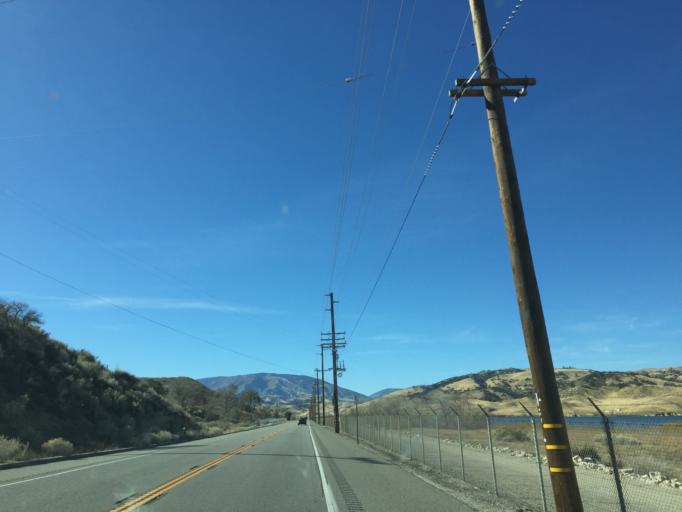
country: US
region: California
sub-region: Kern County
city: Lebec
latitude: 34.7686
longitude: -118.7440
